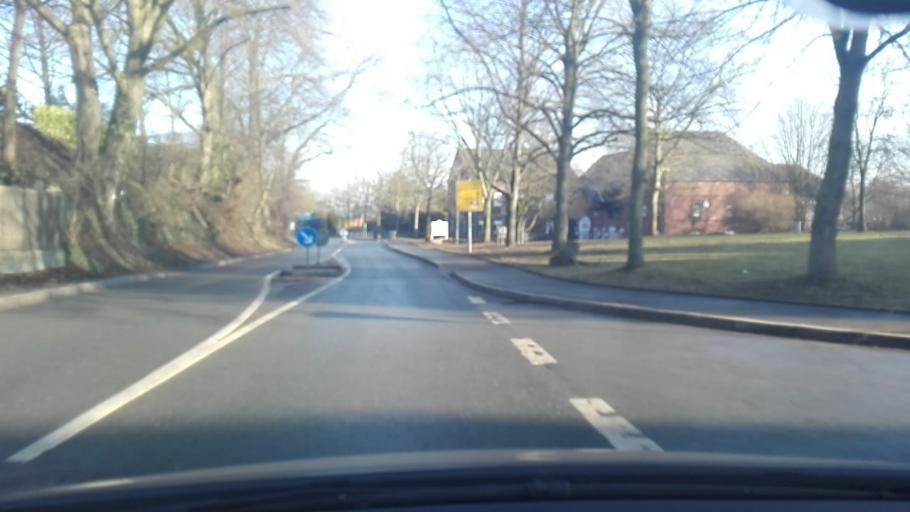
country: DE
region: North Rhine-Westphalia
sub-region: Regierungsbezirk Arnsberg
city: Frondenberg
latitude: 51.5148
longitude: 7.7712
